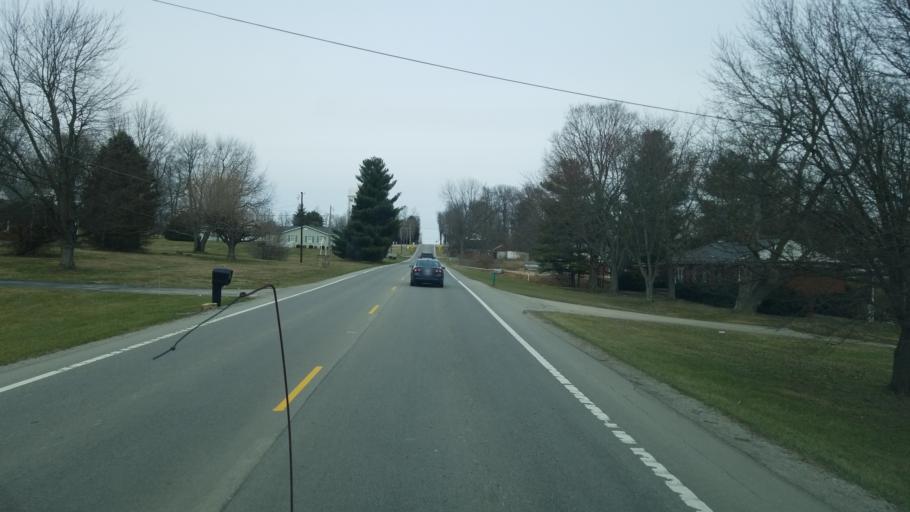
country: US
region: Ohio
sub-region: Highland County
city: Hillsboro
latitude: 39.1323
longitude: -83.6695
